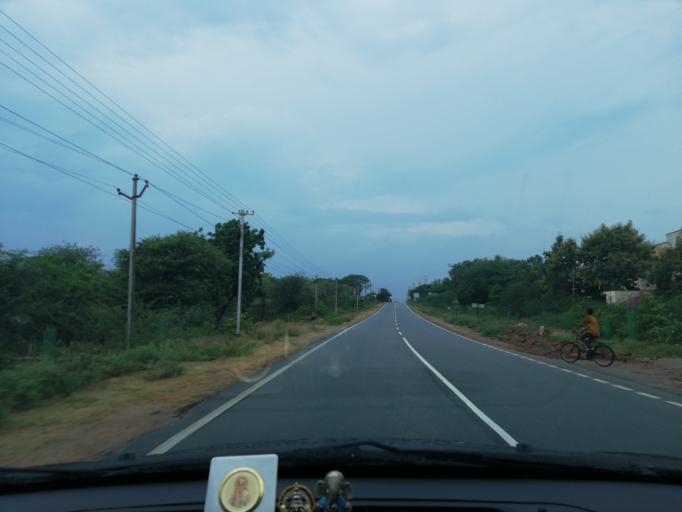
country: IN
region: Andhra Pradesh
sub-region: Guntur
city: Macherla
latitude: 16.6103
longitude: 79.2986
